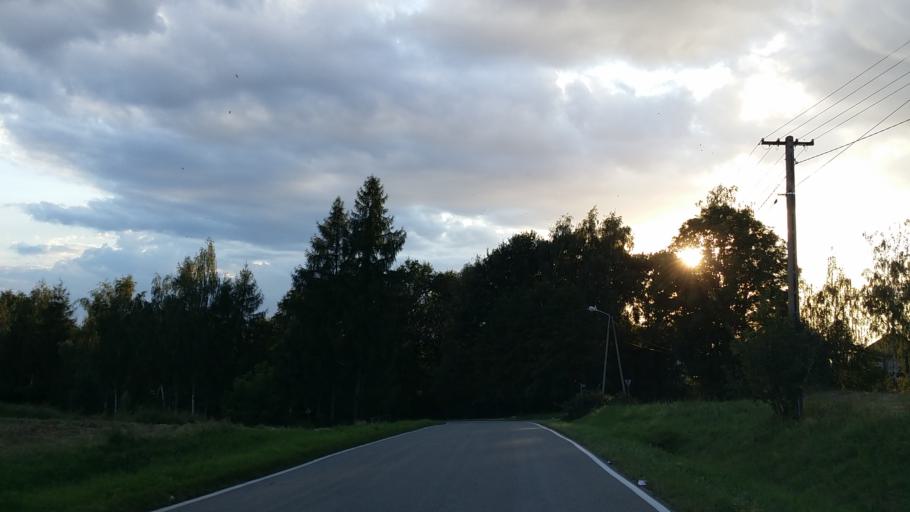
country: PL
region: Lesser Poland Voivodeship
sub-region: Powiat oswiecimski
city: Malec
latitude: 49.9236
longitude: 19.2483
